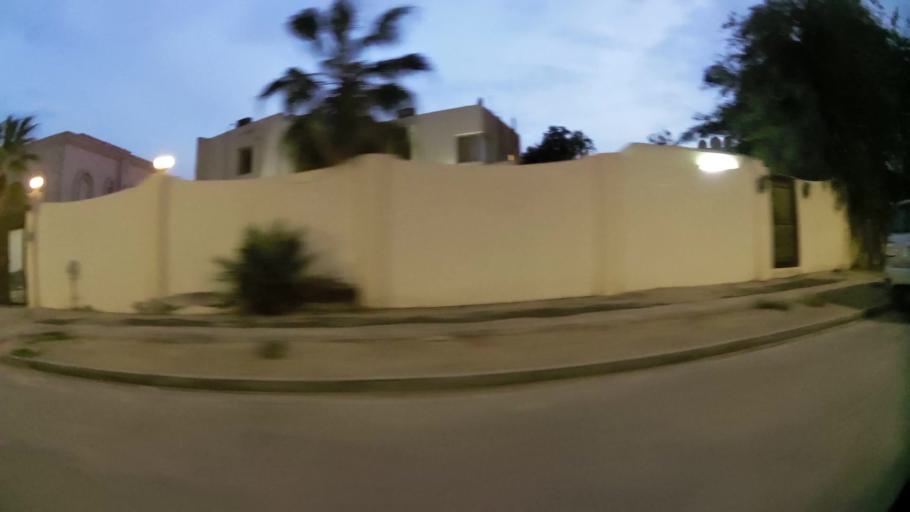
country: QA
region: Baladiyat ad Dawhah
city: Doha
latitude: 25.3432
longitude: 51.5072
